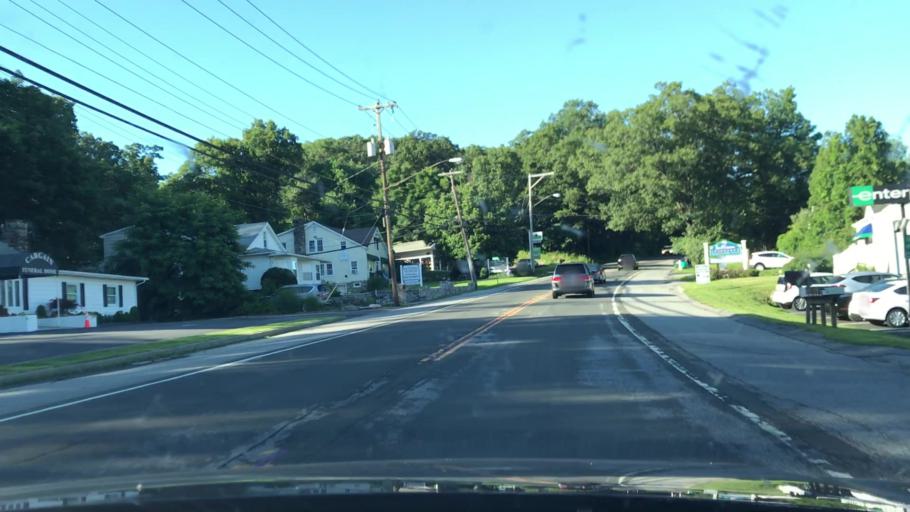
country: US
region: New York
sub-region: Putnam County
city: Mahopac
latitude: 41.3622
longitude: -73.7466
